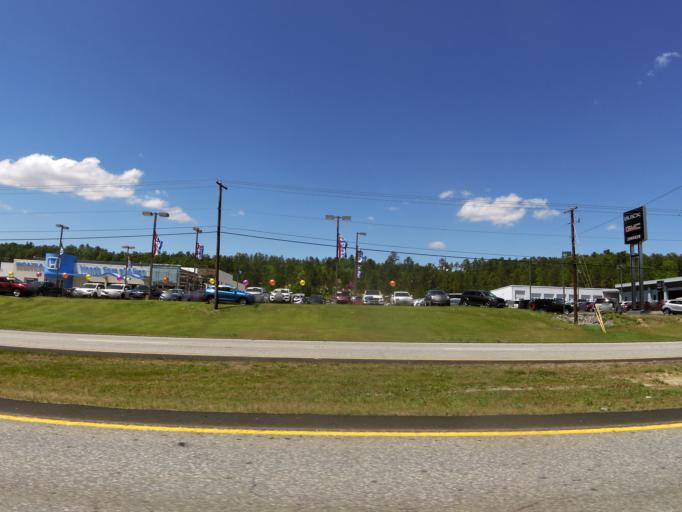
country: US
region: South Carolina
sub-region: Aiken County
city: Warrenville
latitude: 33.5587
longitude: -81.7923
